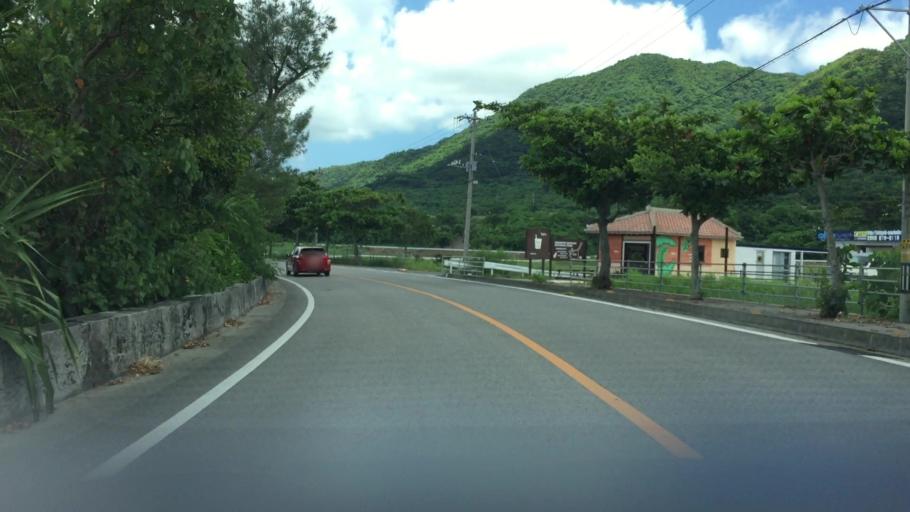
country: JP
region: Okinawa
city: Ishigaki
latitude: 24.4132
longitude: 124.1436
